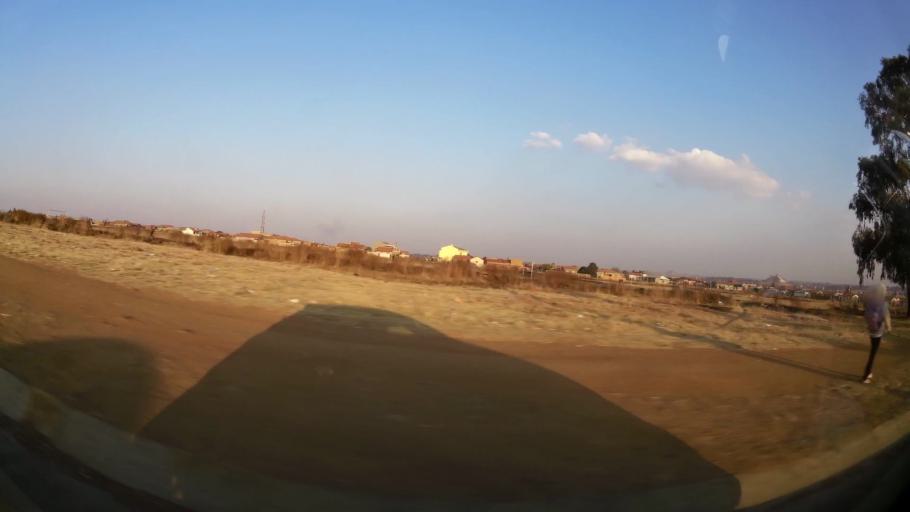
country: ZA
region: Gauteng
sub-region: Ekurhuleni Metropolitan Municipality
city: Benoni
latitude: -26.1588
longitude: 28.3750
